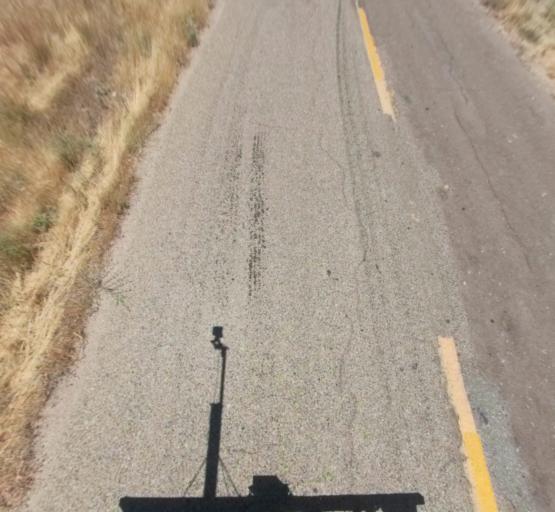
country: US
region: California
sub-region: Madera County
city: Fairmead
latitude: 37.0256
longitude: -120.1750
